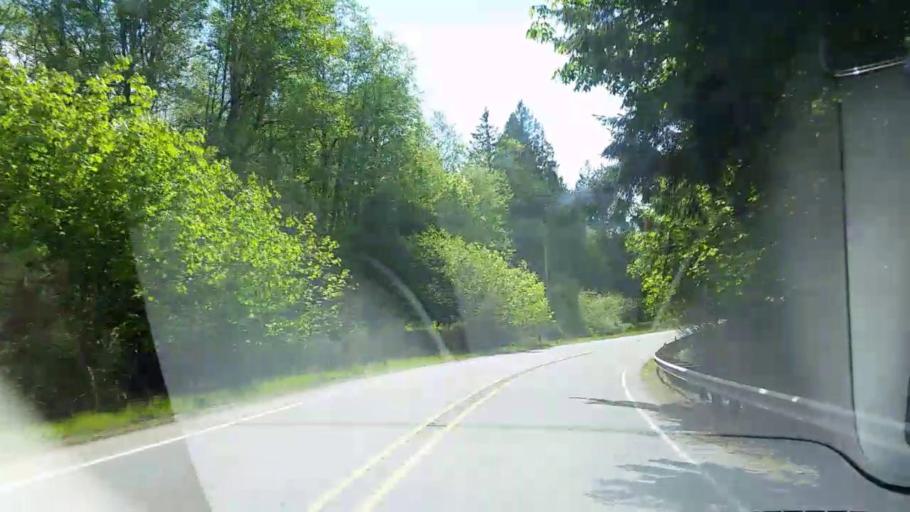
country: US
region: Washington
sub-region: Pierce County
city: Key Center
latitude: 47.3722
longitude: -122.7803
